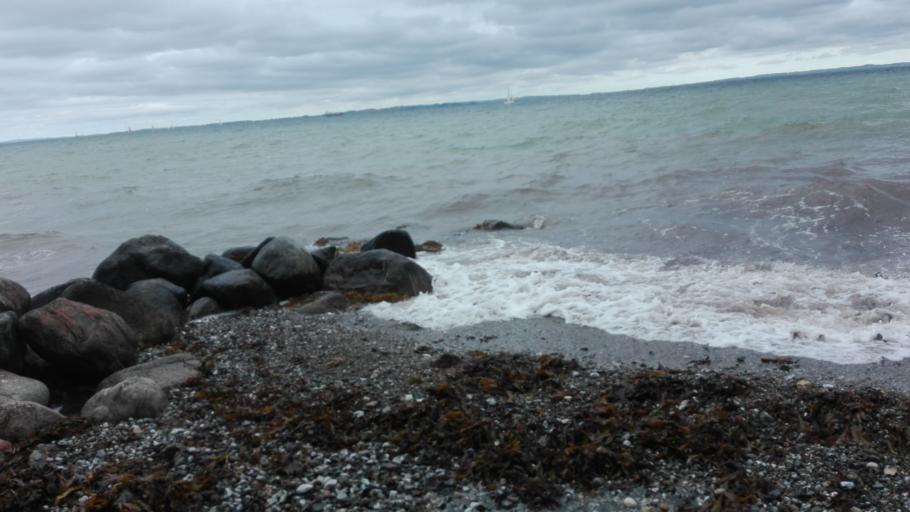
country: DK
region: Central Jutland
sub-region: Arhus Kommune
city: Beder
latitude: 56.1029
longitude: 10.2374
